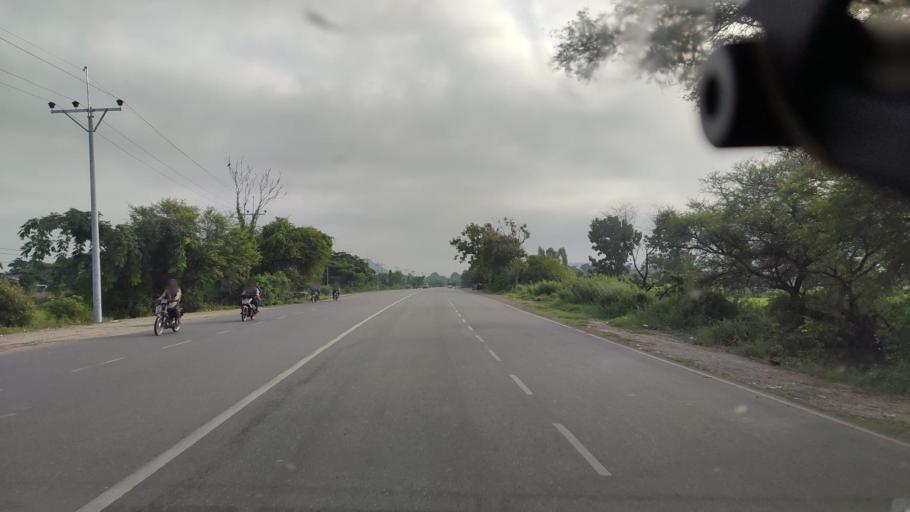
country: MM
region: Mandalay
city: Mandalay
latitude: 22.0728
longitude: 96.1393
